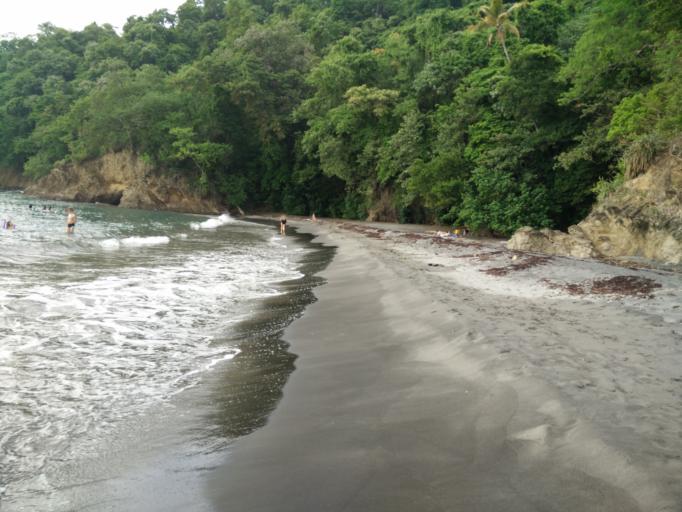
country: MQ
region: Martinique
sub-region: Martinique
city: Basse-Pointe
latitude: 14.8428
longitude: -61.2189
